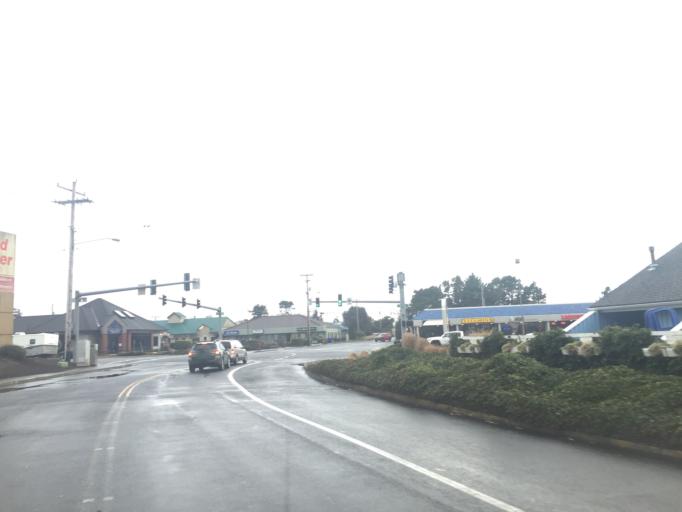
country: US
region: Oregon
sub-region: Lincoln County
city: Newport
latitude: 44.6517
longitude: -124.0523
